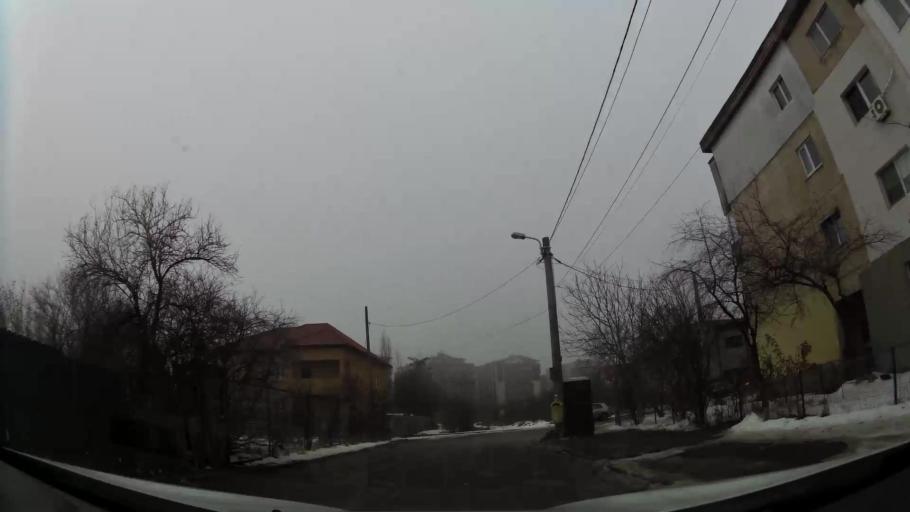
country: RO
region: Ilfov
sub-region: Comuna Chiajna
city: Rosu
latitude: 44.4415
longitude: 26.0036
